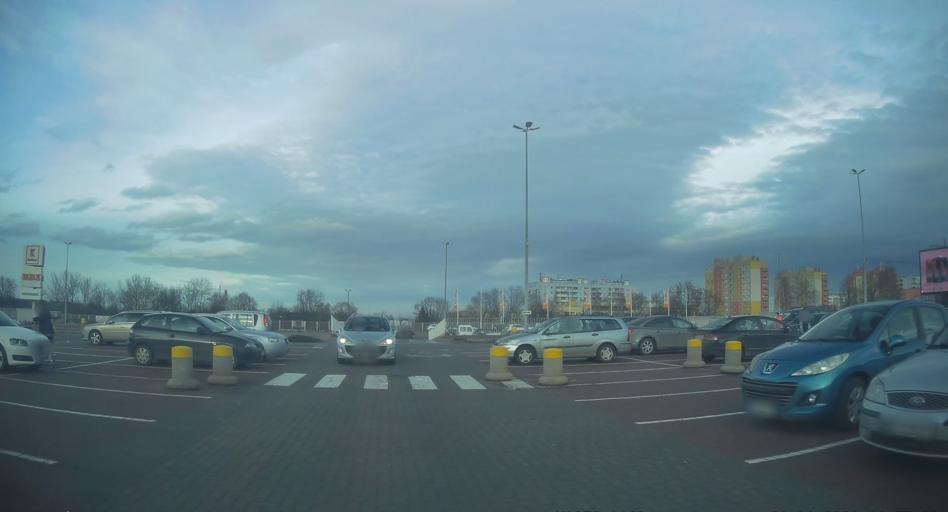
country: PL
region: Lesser Poland Voivodeship
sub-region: Powiat krakowski
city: Ochojno
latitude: 50.0144
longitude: 19.9938
